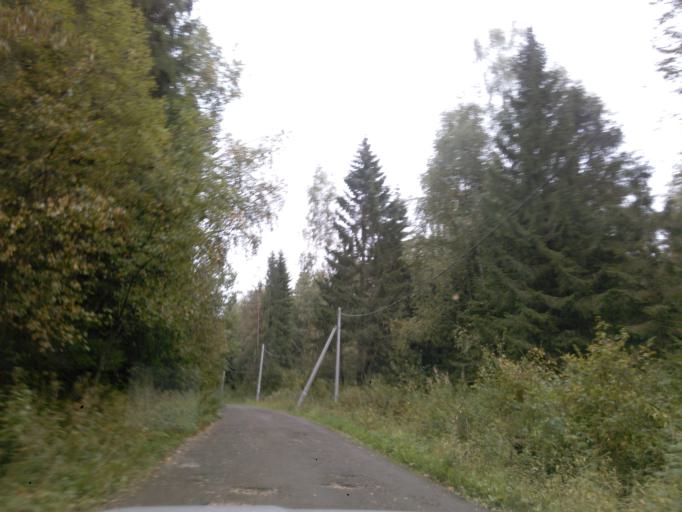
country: RU
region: Moskovskaya
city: Mendeleyevo
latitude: 56.0913
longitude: 37.2610
